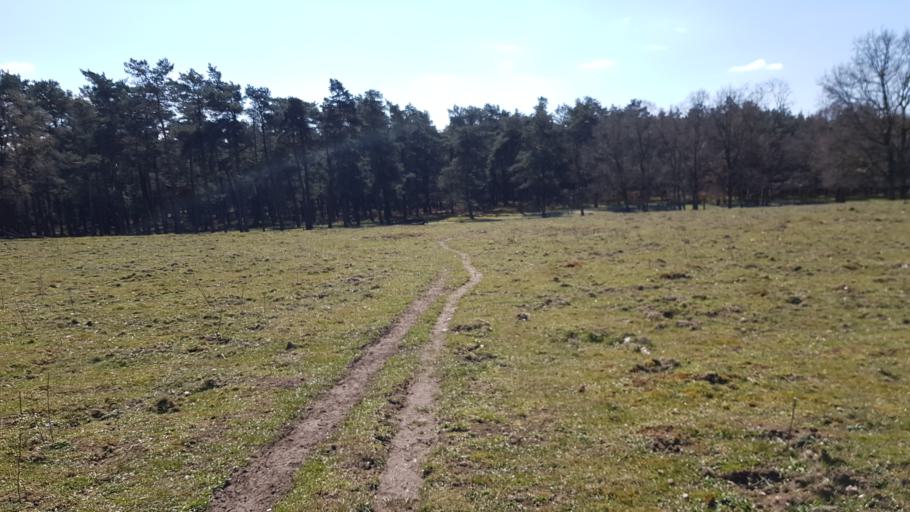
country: NL
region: Gelderland
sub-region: Gemeente Rozendaal
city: Rozendaal
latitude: 52.0743
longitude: 5.9563
